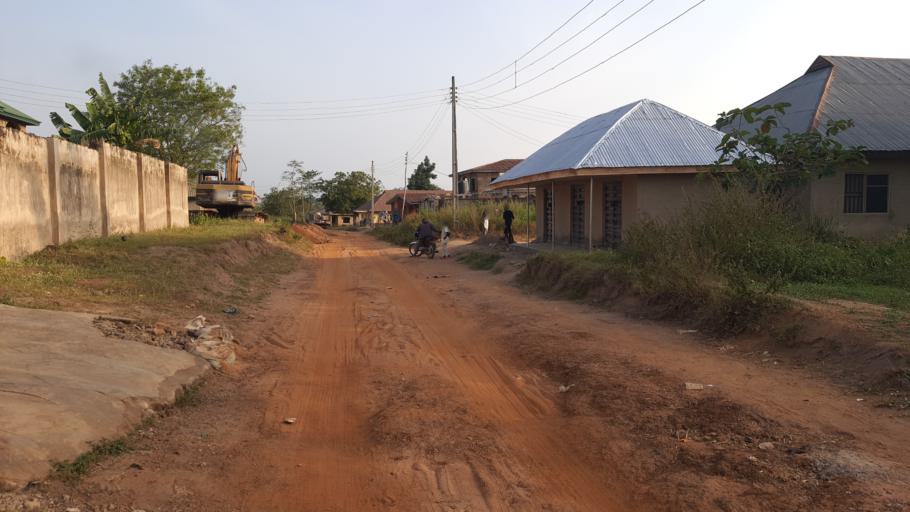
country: NG
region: Osun
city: Iwo
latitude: 7.6228
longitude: 4.1590
